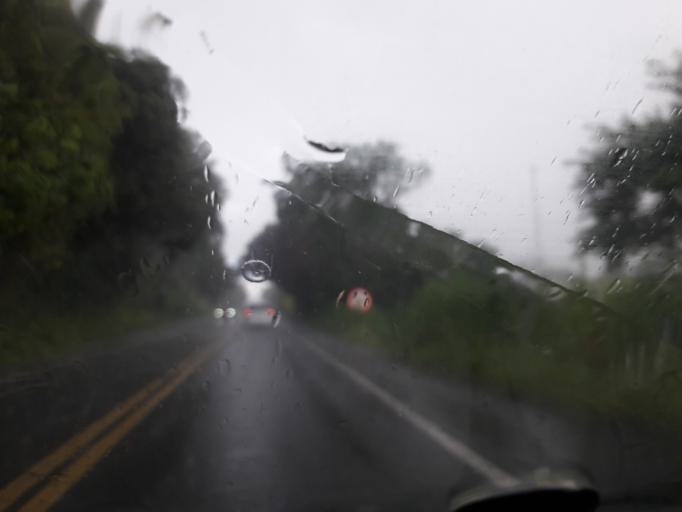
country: BR
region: Sao Paulo
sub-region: Bom Jesus Dos Perdoes
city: Bom Jesus dos Perdoes
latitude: -23.1802
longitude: -46.4026
